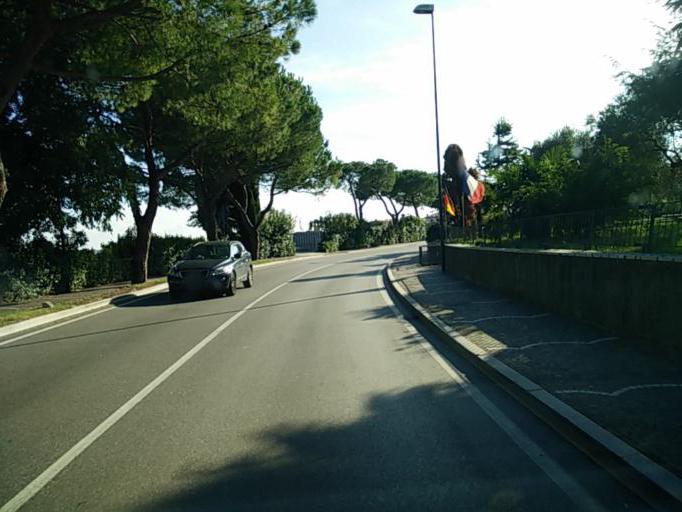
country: IT
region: Lombardy
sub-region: Provincia di Brescia
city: Sirmione
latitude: 45.4744
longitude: 10.6109
